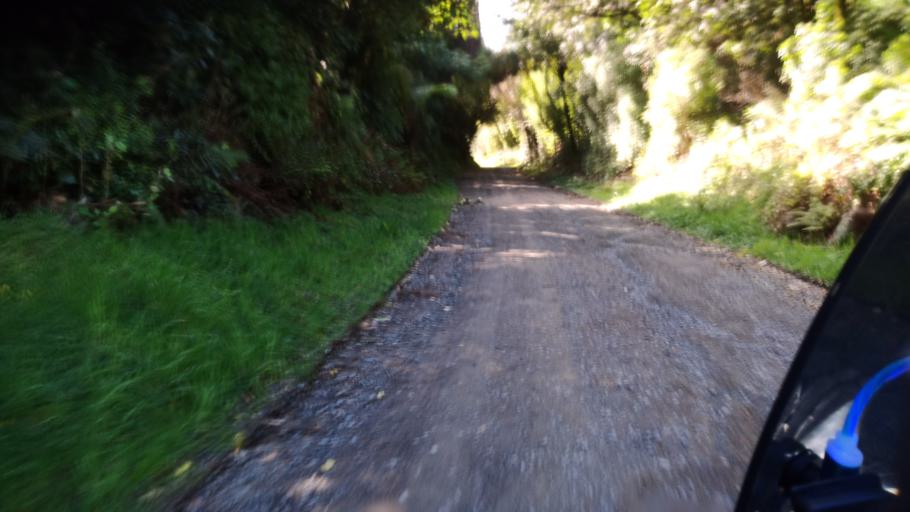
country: NZ
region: Hawke's Bay
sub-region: Wairoa District
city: Wairoa
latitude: -38.7997
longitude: 177.1212
